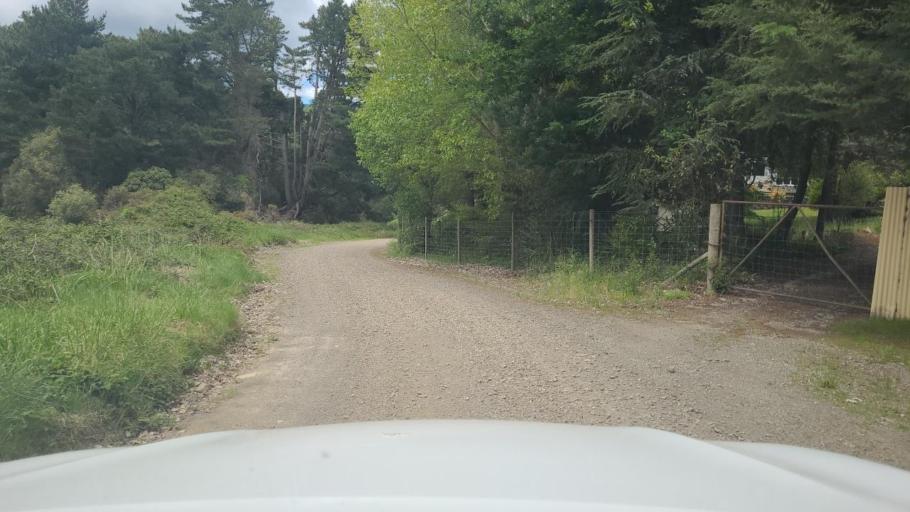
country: NZ
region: Hawke's Bay
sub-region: Napier City
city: Taradale
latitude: -39.1819
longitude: 176.6332
